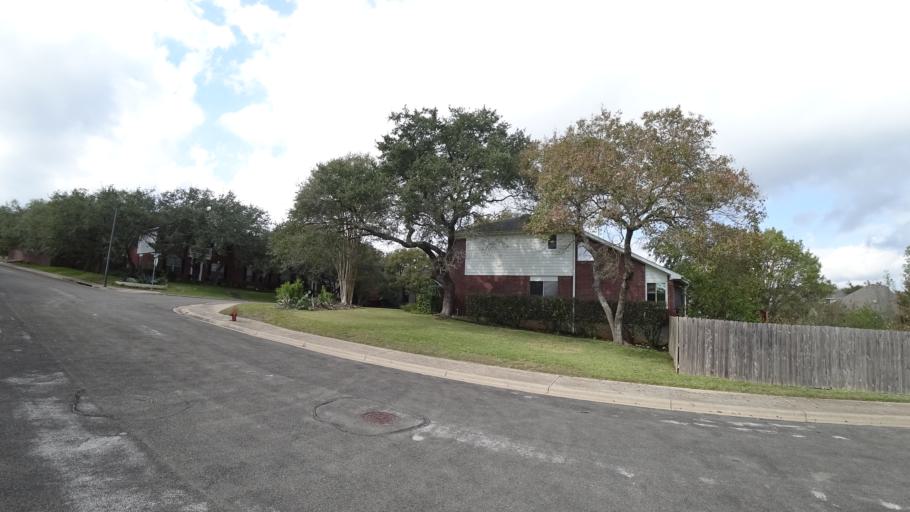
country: US
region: Texas
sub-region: Williamson County
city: Anderson Mill
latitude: 30.4217
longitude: -97.8592
